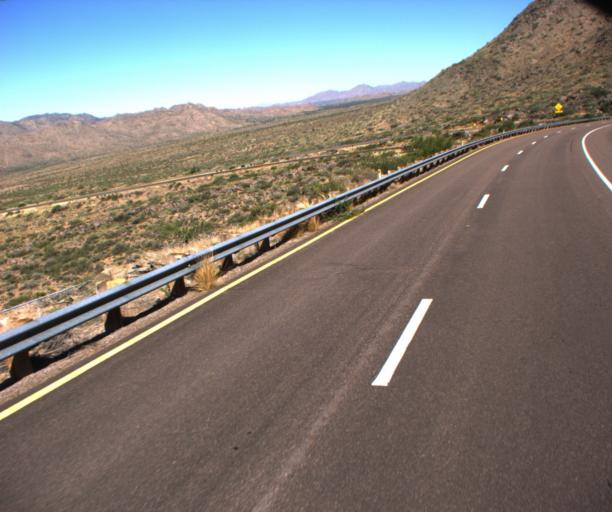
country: US
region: Arizona
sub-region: Yavapai County
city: Congress
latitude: 34.2059
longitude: -112.7976
